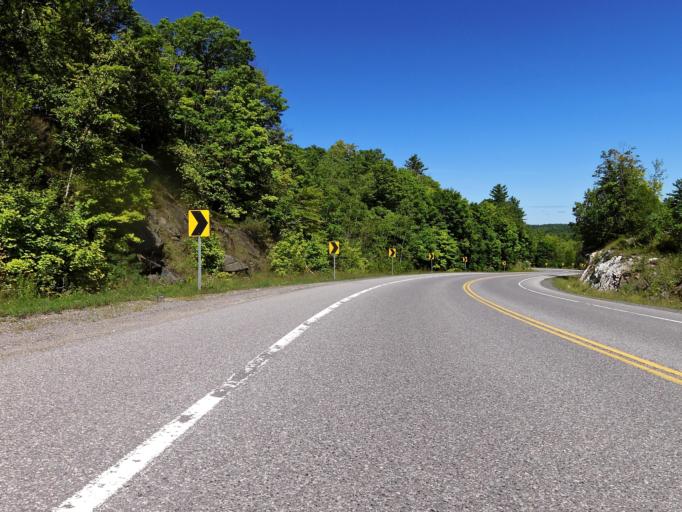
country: CA
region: Ontario
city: Arnprior
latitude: 45.1560
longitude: -76.5187
